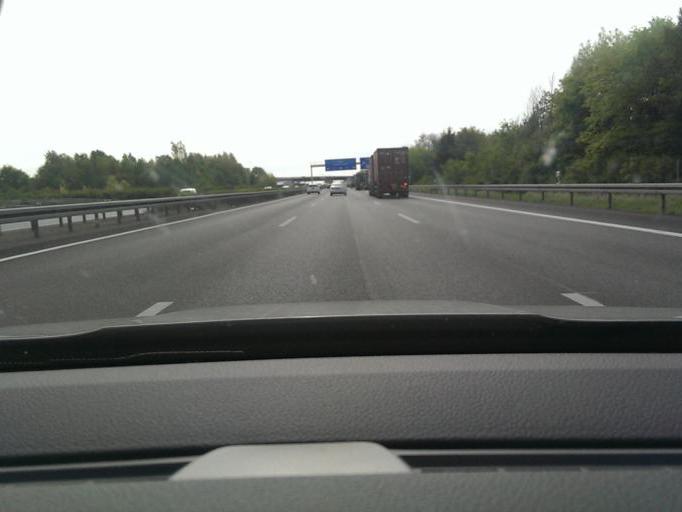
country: DE
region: Lower Saxony
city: Klein Schwulper
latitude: 52.3268
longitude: 10.4654
